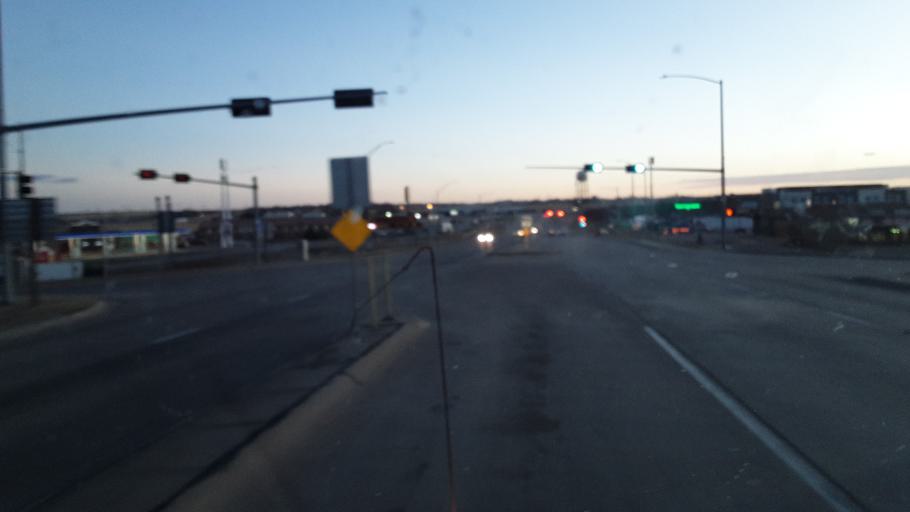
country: US
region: Nebraska
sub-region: Keith County
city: Ogallala
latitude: 41.1141
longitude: -101.7154
